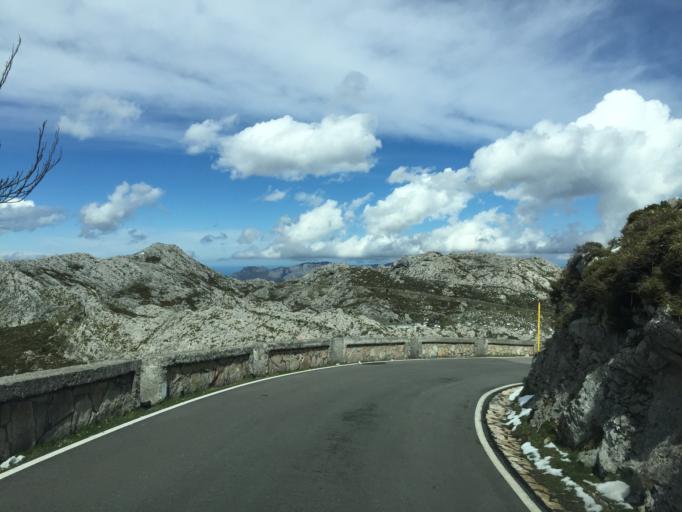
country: ES
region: Asturias
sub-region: Province of Asturias
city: Amieva
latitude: 43.2767
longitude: -5.0055
